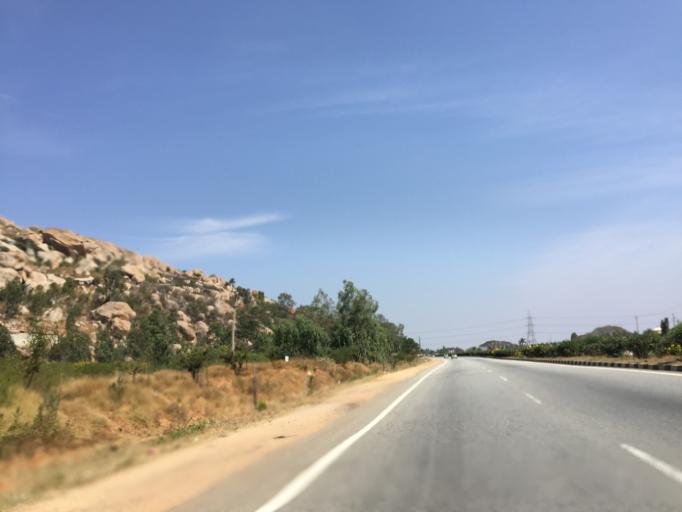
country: IN
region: Karnataka
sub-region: Kolar
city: Kolar
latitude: 13.1209
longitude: 78.0957
